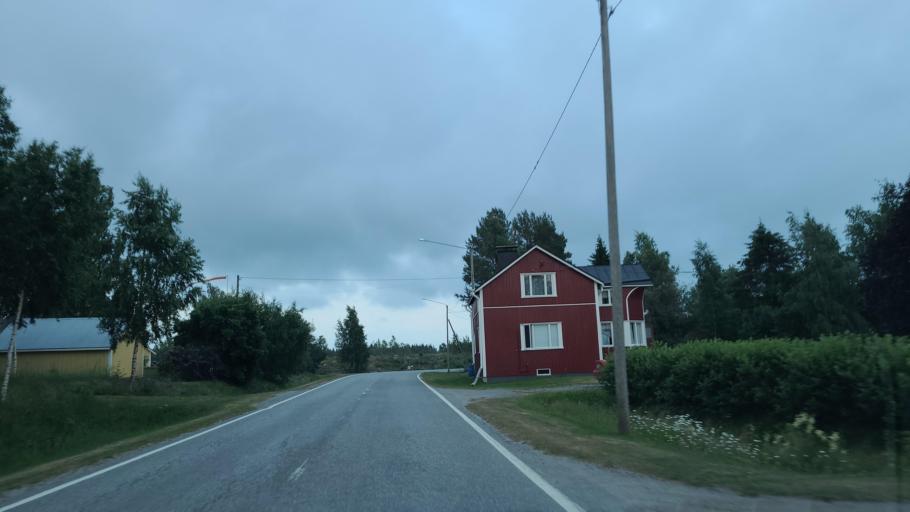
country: FI
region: Ostrobothnia
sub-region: Vaasa
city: Replot
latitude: 63.2837
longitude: 21.1246
